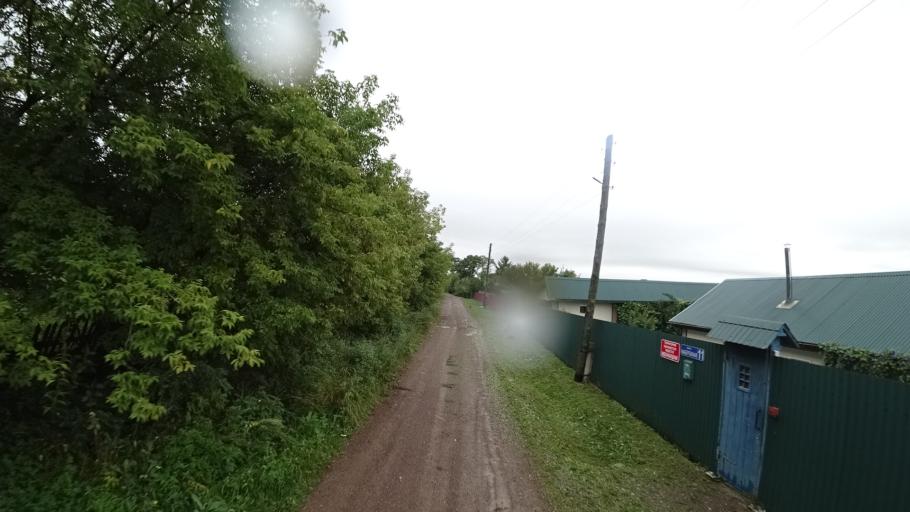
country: RU
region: Primorskiy
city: Monastyrishche
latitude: 44.2646
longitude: 132.4043
